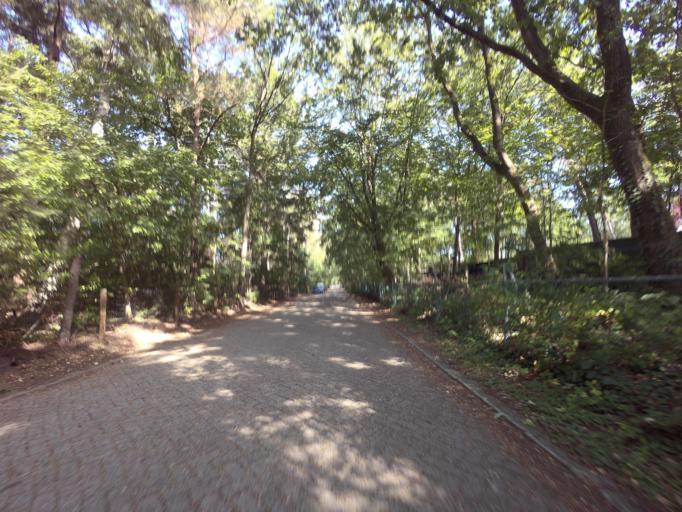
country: NL
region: Gelderland
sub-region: Gemeente Apeldoorn
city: Loenen
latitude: 52.1452
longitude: 6.0341
